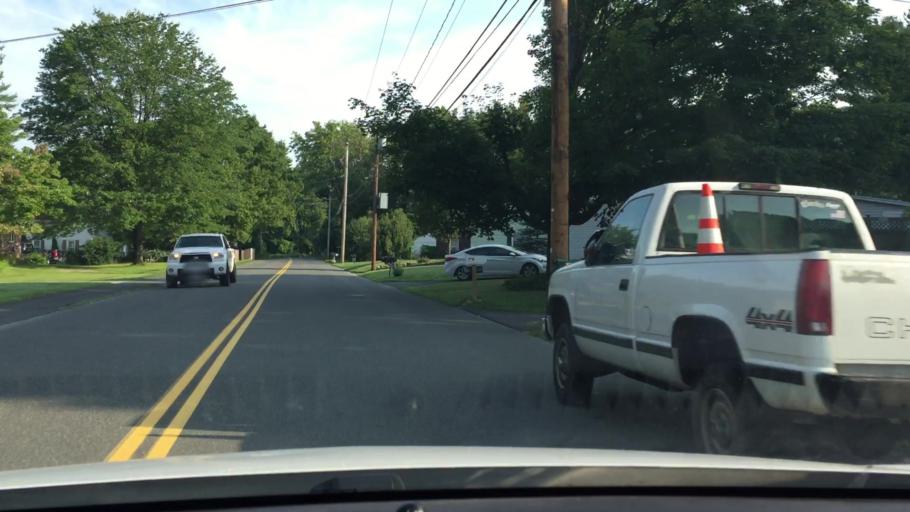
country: US
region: Massachusetts
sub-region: Berkshire County
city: Lee
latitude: 42.3235
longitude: -73.2384
